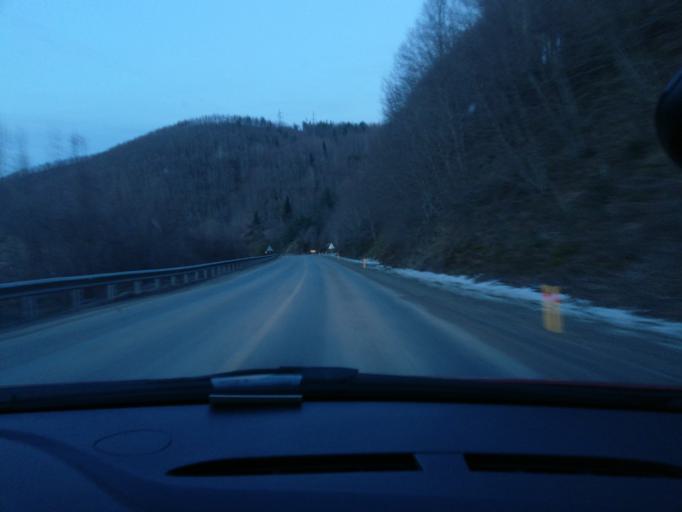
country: TR
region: Kastamonu
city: Inebolu
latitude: 41.9102
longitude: 33.7235
